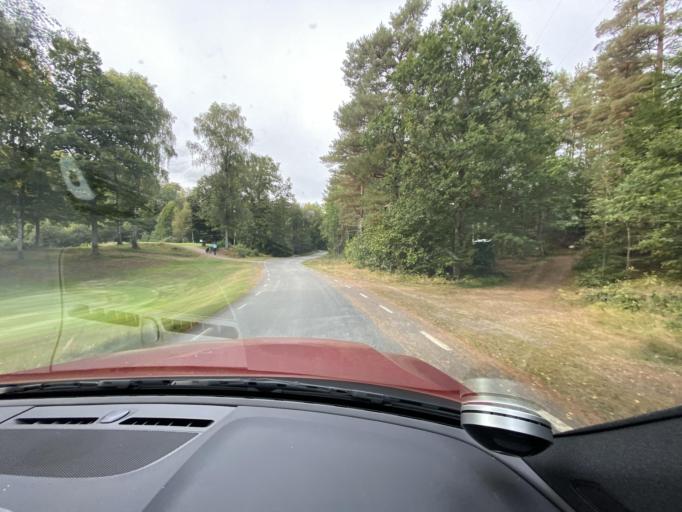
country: SE
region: Skane
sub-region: Hassleholms Kommun
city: Bjarnum
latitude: 56.3500
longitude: 13.7088
